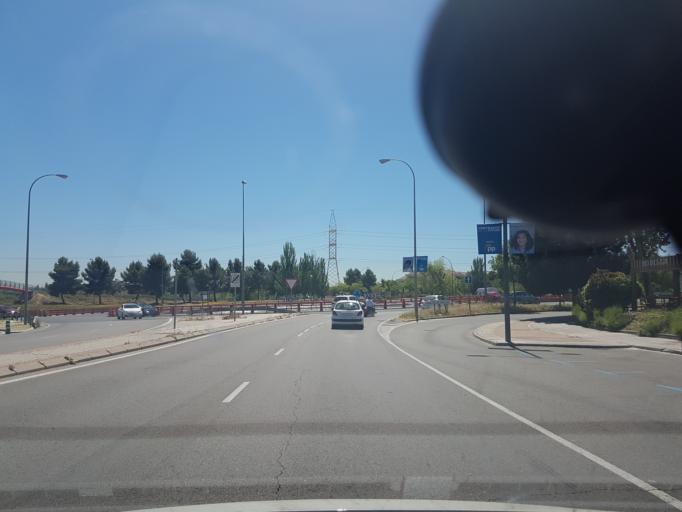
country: ES
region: Madrid
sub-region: Provincia de Madrid
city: Pozuelo de Alarcon
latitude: 40.4345
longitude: -3.7978
